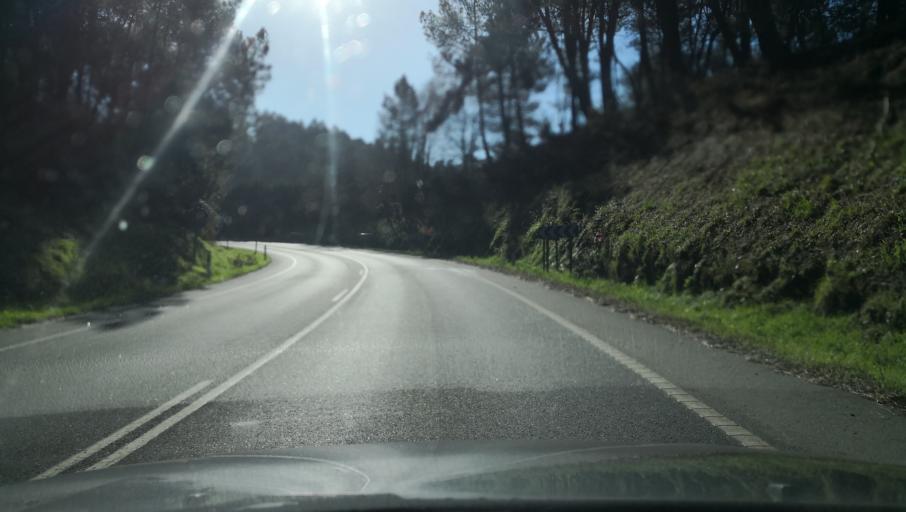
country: ES
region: Galicia
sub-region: Provincia de Pontevedra
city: Silleda
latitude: 42.7307
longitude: -8.3185
